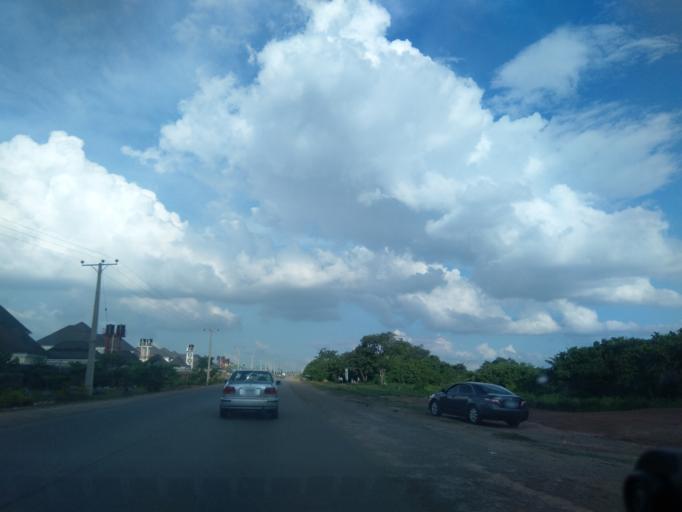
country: NG
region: Abuja Federal Capital Territory
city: Abuja
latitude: 9.0422
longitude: 7.3921
